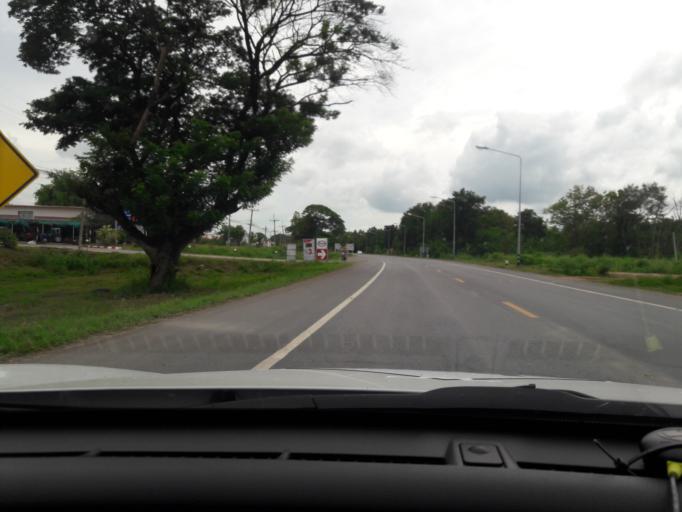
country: TH
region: Nakhon Sawan
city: Tak Fa
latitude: 15.3591
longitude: 100.5030
